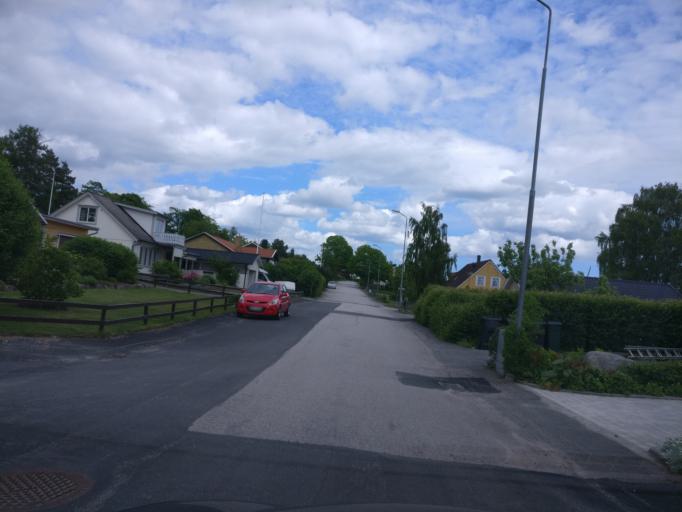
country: SE
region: Kalmar
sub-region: Vasterviks Kommun
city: Vaestervik
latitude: 57.9004
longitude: 16.6890
